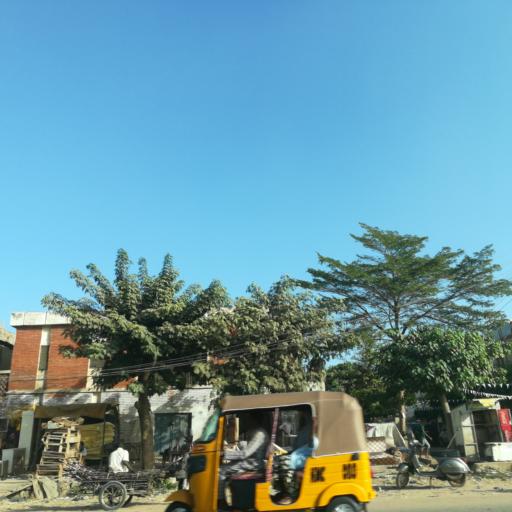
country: NG
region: Kano
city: Kano
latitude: 12.0108
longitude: 8.4984
